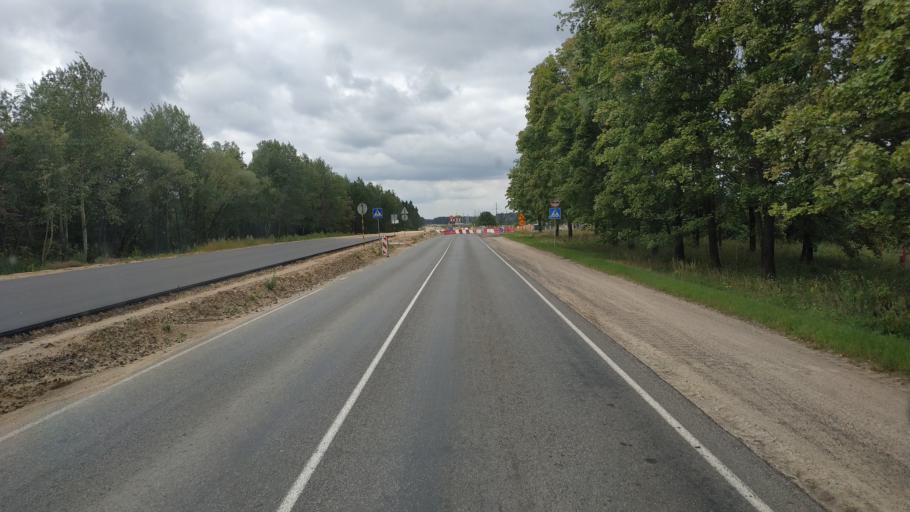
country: BY
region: Mogilev
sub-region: Mahilyowski Rayon
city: Kadino
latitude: 53.8704
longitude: 30.4601
